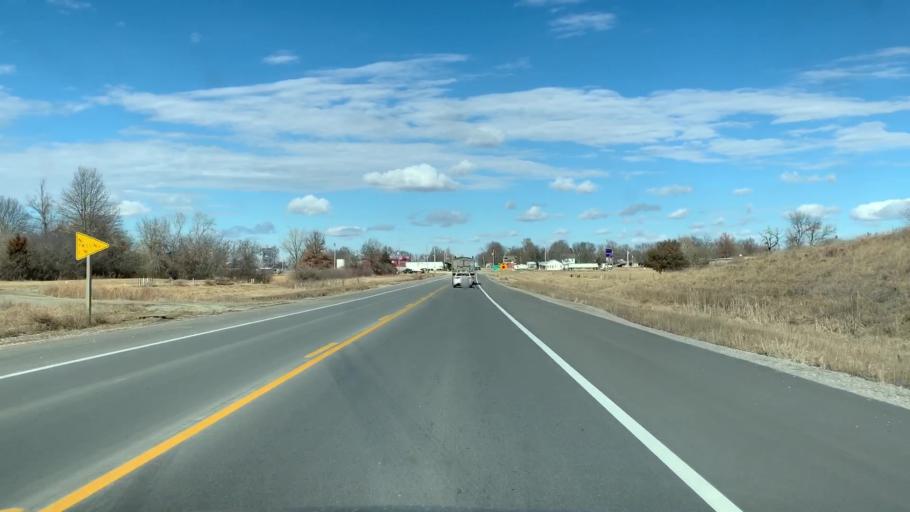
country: US
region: Kansas
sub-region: Crawford County
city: Pittsburg
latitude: 37.3364
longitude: -94.8322
